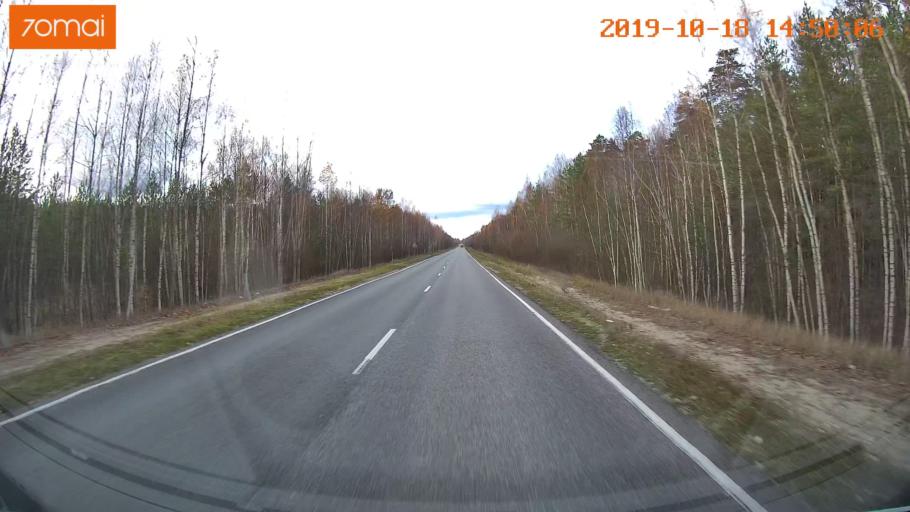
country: RU
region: Vladimir
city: Kurlovo
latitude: 55.4227
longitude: 40.6462
